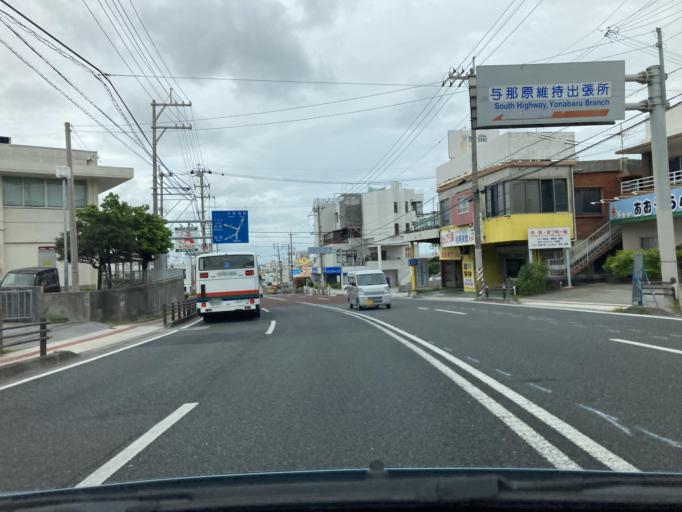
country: JP
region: Okinawa
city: Ginowan
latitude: 26.2004
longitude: 127.7517
